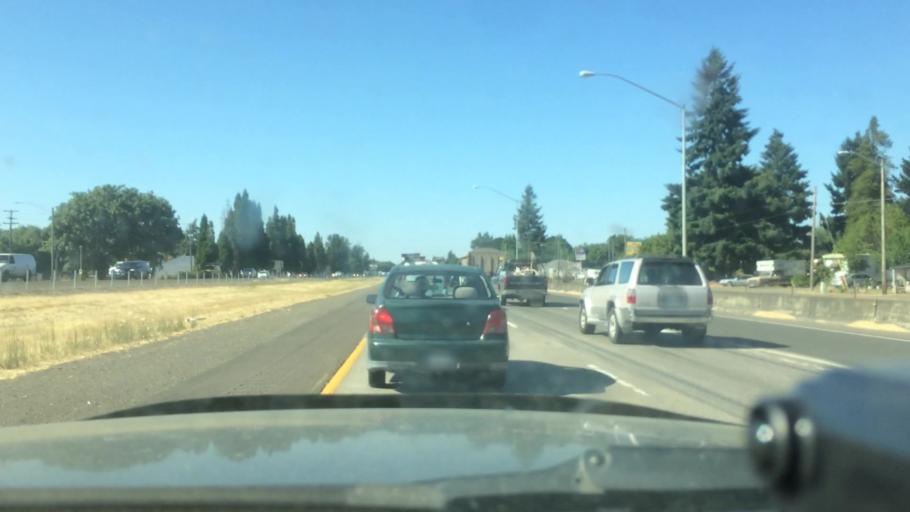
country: US
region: Oregon
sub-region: Linn County
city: Millersburg
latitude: 44.6508
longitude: -123.0615
